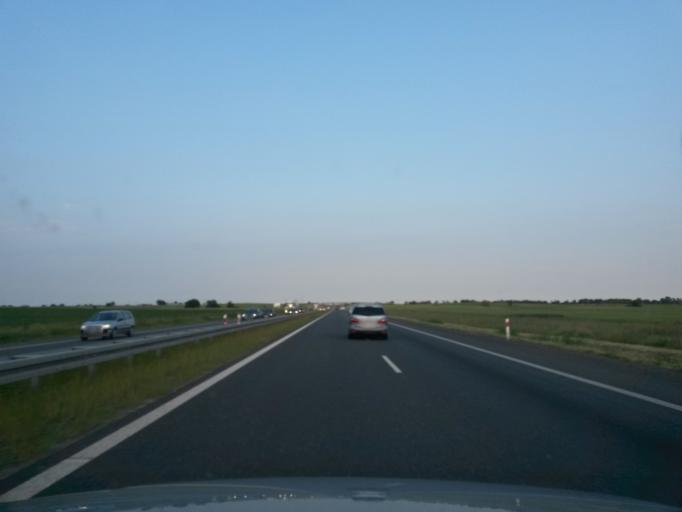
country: PL
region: Lower Silesian Voivodeship
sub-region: Powiat olesnicki
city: Sycow
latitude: 51.3019
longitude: 17.6393
